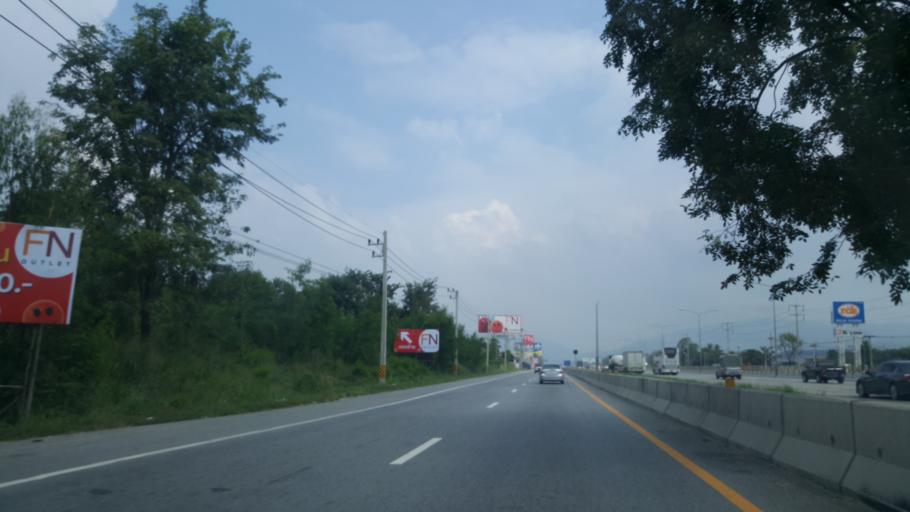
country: TH
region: Chon Buri
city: Si Racha
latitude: 13.1871
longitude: 100.9972
